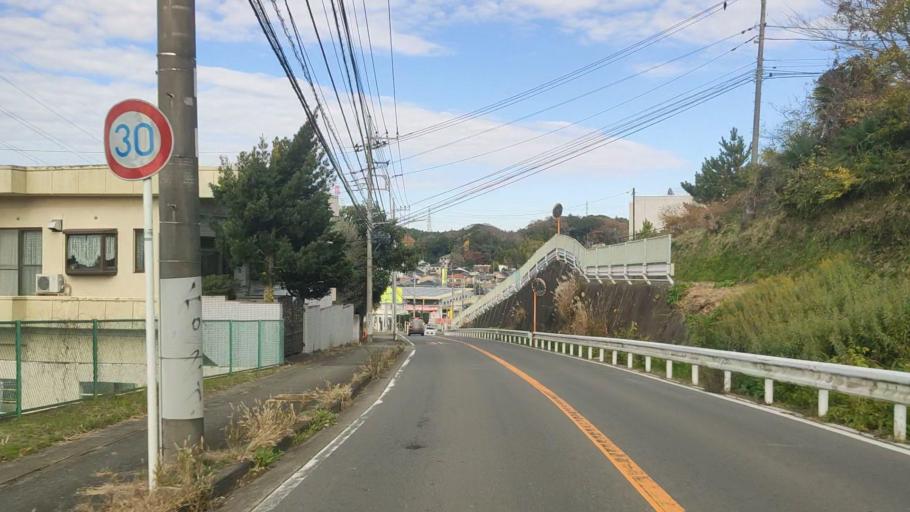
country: JP
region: Kanagawa
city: Minami-rinkan
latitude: 35.4917
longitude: 139.5063
